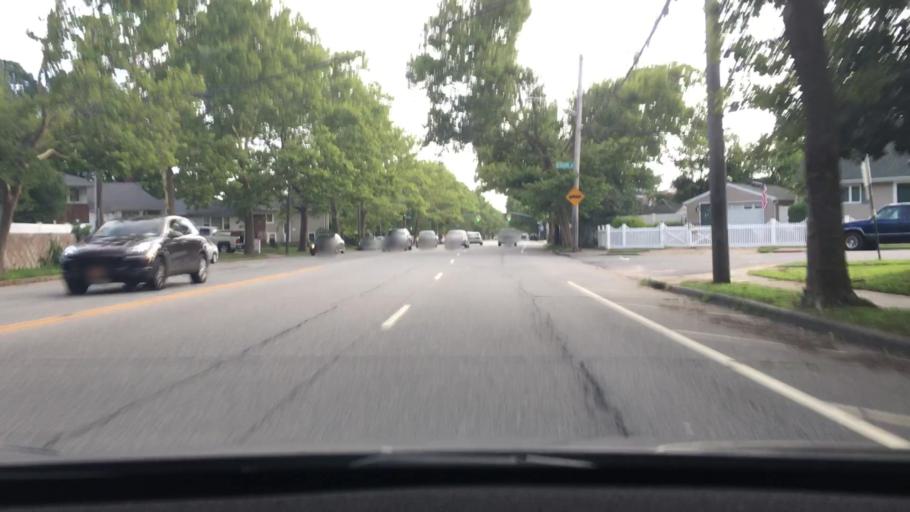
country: US
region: New York
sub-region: Nassau County
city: Hicksville
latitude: 40.7784
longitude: -73.5087
